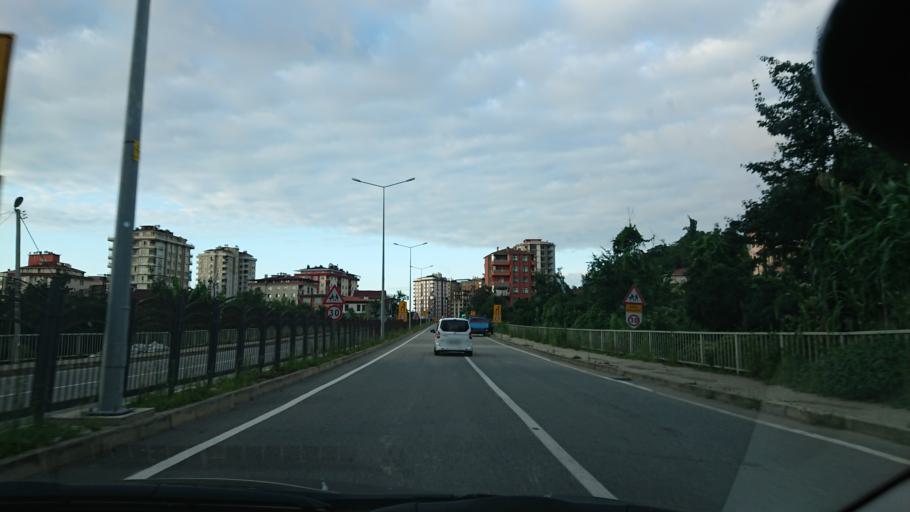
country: TR
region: Rize
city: Gundogdu
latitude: 41.0339
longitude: 40.5631
